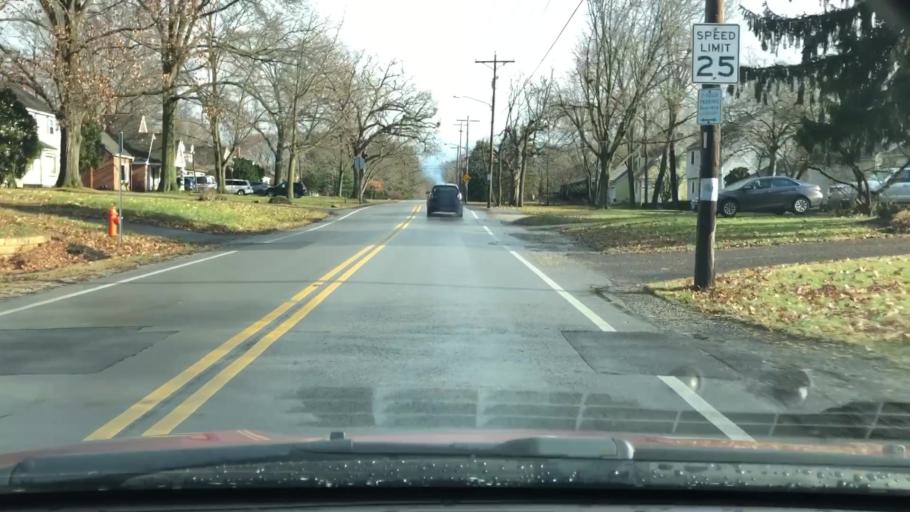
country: US
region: Ohio
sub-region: Franklin County
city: Worthington
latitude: 40.0494
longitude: -83.0146
